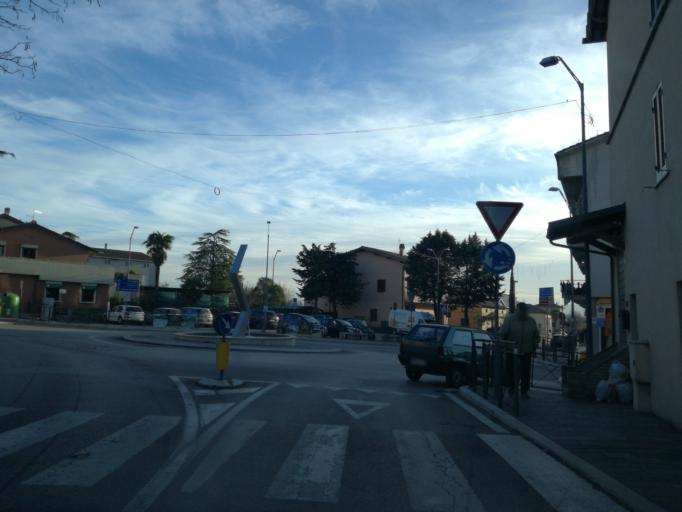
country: IT
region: Umbria
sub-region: Provincia di Perugia
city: Rivotorto
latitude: 43.0443
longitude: 12.6174
